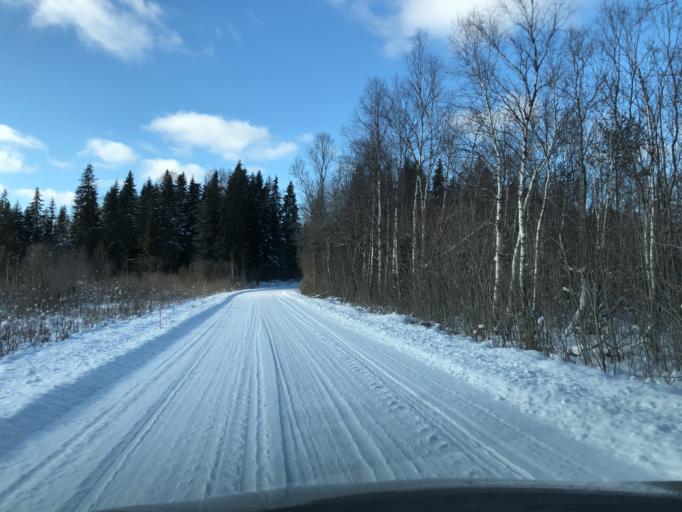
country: EE
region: Jaervamaa
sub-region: Paide linn
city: Paide
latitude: 59.0580
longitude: 25.5058
